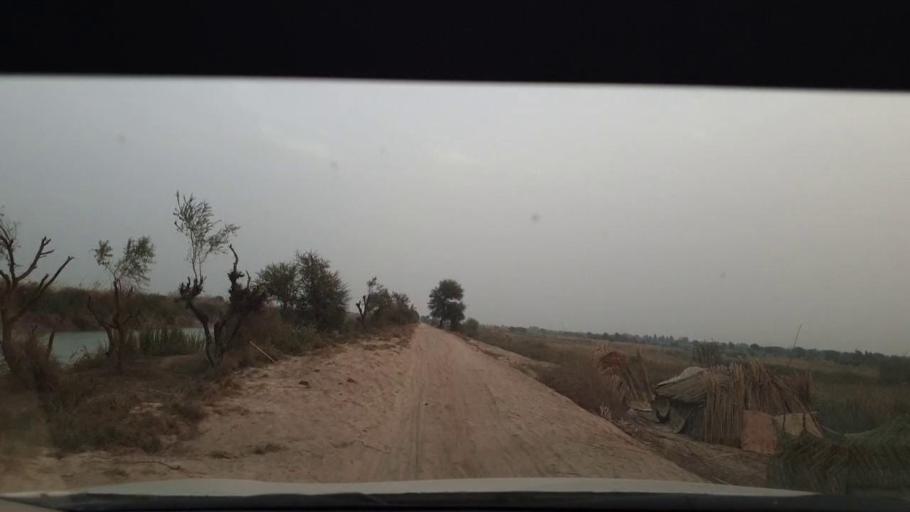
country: PK
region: Sindh
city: Berani
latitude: 25.8636
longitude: 68.7740
